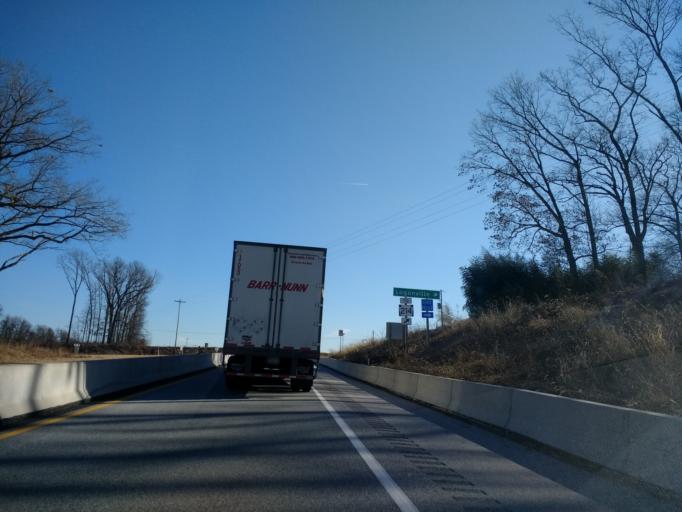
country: US
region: Pennsylvania
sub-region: York County
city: Loganville
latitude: 39.8660
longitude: -76.7001
